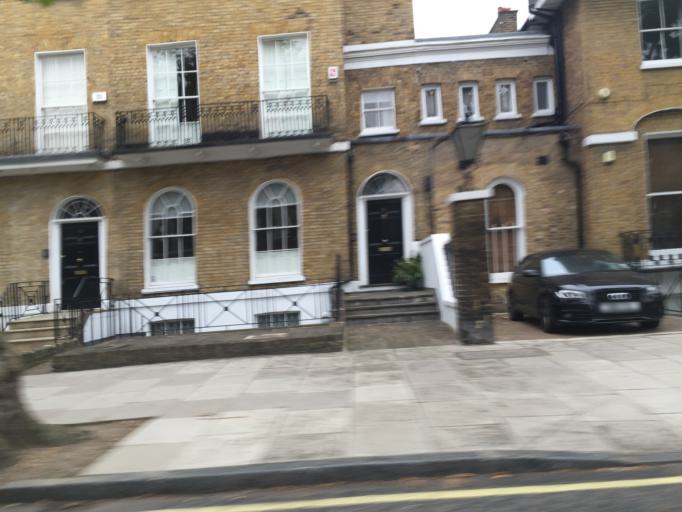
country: GB
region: England
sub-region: Greater London
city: Bayswater
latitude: 51.5271
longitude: -0.1772
